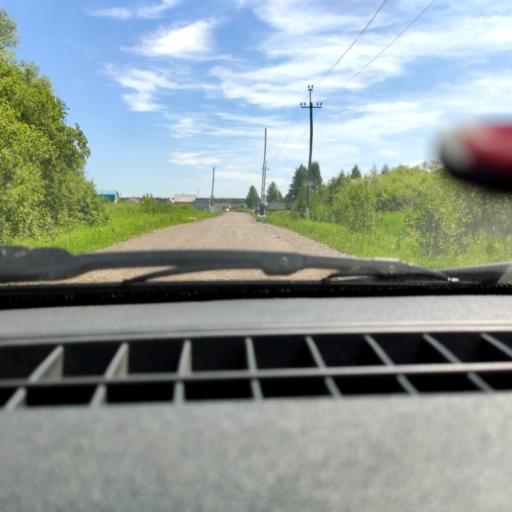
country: RU
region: Bashkortostan
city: Kabakovo
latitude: 54.7274
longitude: 56.2054
